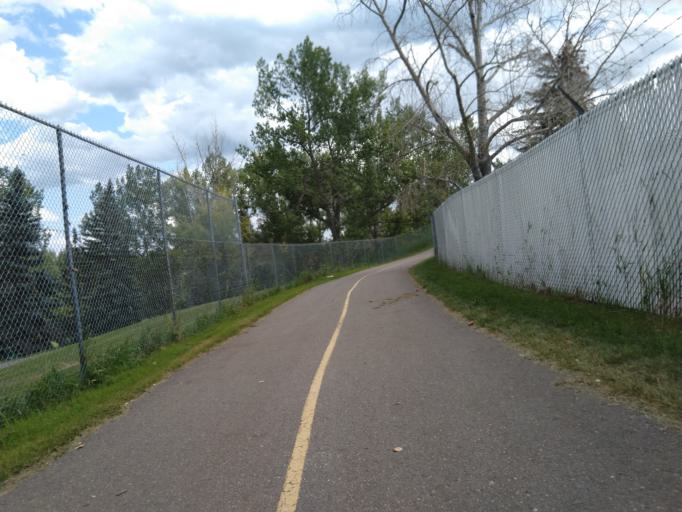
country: CA
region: Alberta
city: Calgary
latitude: 51.0770
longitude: -114.0993
